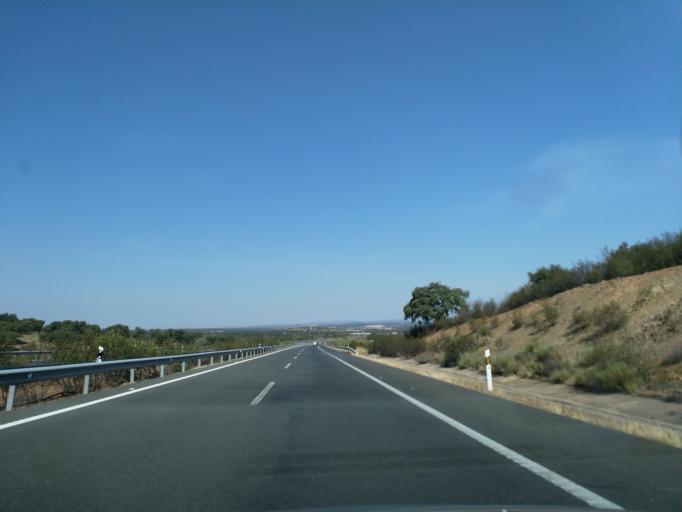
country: ES
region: Extremadura
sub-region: Provincia de Caceres
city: Alcuescar
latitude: 39.1788
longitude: -6.2731
